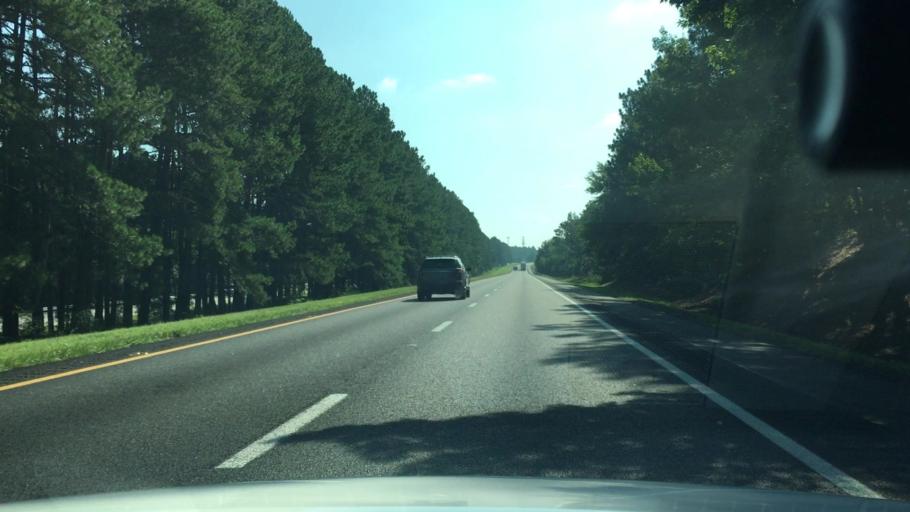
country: US
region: South Carolina
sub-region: Aiken County
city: Graniteville
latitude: 33.6301
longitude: -81.7993
